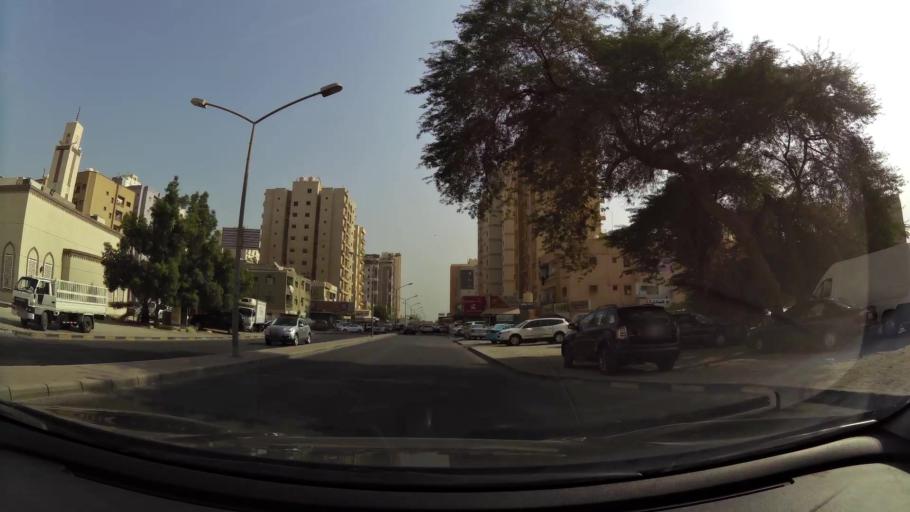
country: KW
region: Muhafazat Hawalli
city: As Salimiyah
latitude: 29.3244
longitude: 48.0587
